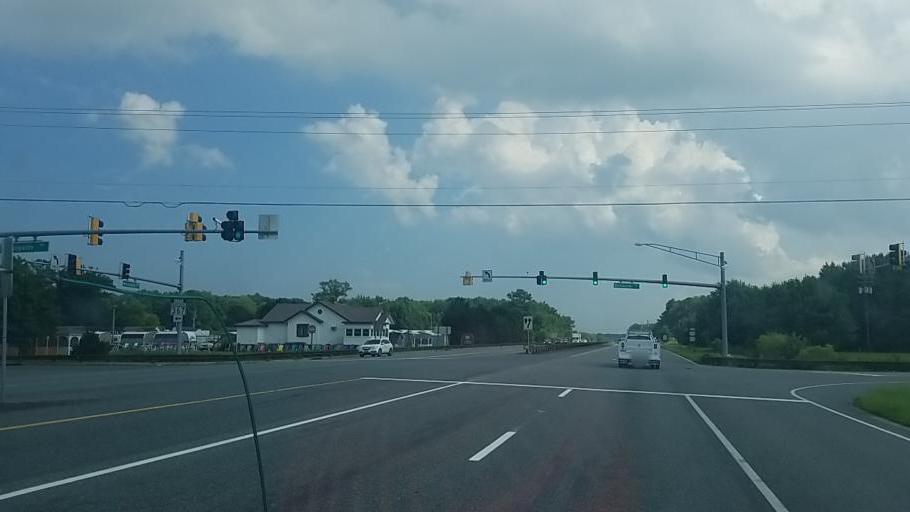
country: US
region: Delaware
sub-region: Sussex County
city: Selbyville
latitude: 38.4290
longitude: -75.2199
